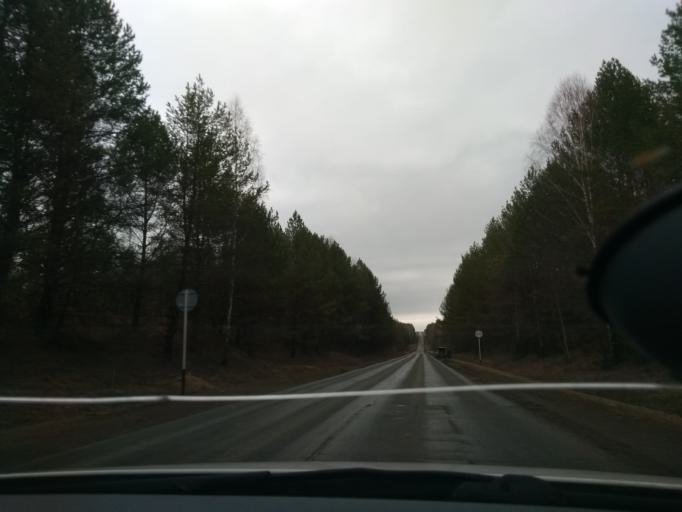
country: RU
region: Perm
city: Kungur
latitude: 57.3679
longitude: 56.8287
